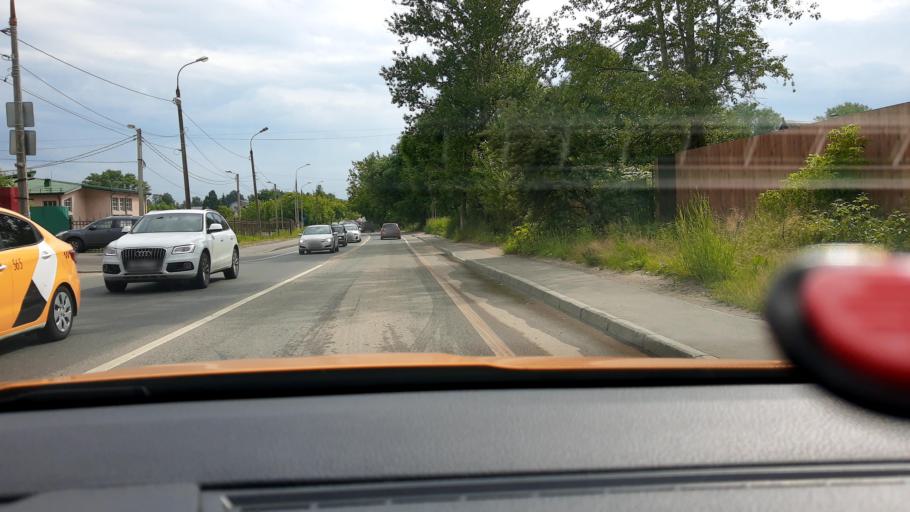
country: RU
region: Moskovskaya
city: Pirogovskiy
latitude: 55.9798
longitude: 37.7260
